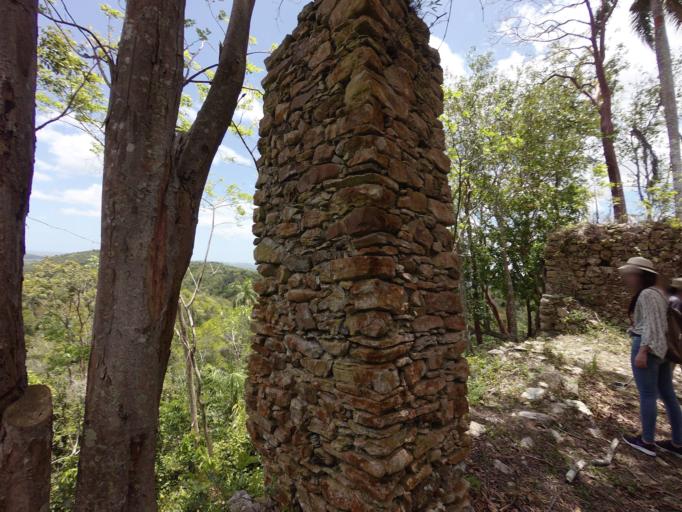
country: CU
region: Artemisa
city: Soroa
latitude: 22.8624
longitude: -82.9274
